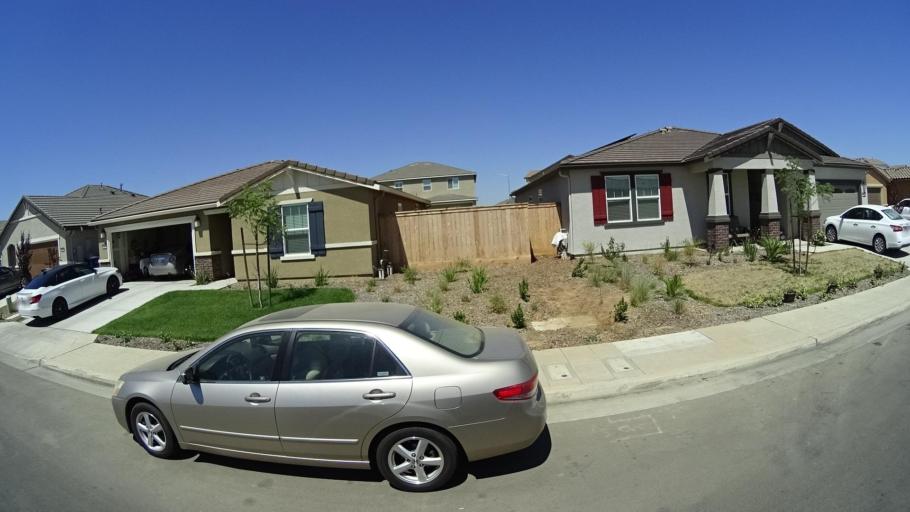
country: US
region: California
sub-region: Fresno County
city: Sunnyside
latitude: 36.7237
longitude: -119.6681
